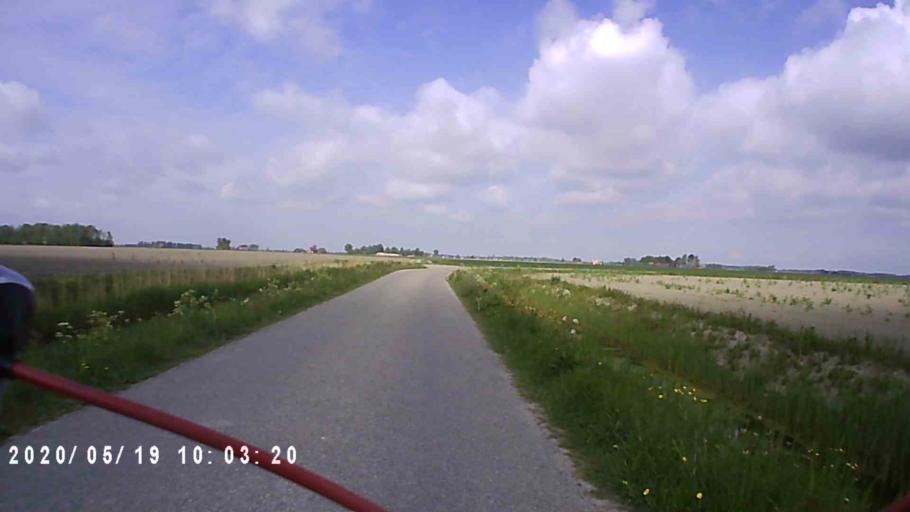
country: NL
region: Friesland
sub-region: Gemeente Kollumerland en Nieuwkruisland
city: Kollum
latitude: 53.3020
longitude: 6.2296
